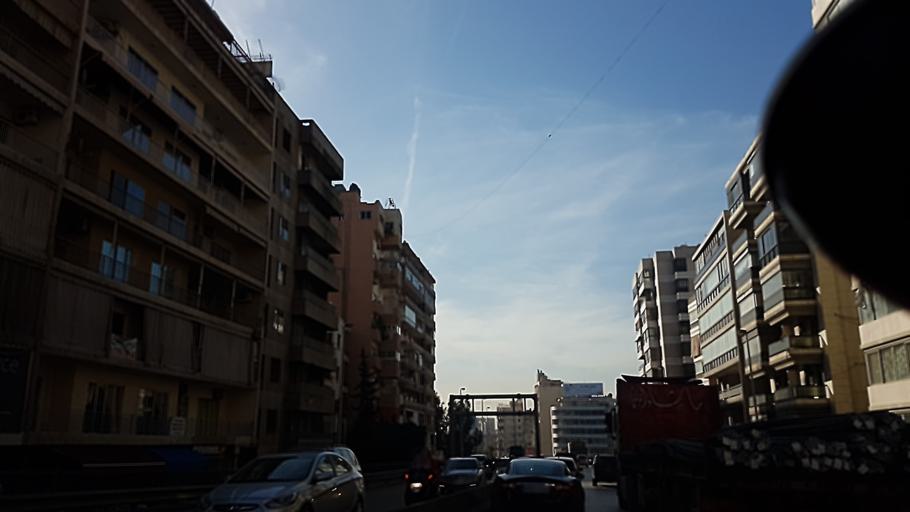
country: LB
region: Beyrouth
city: Beirut
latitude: 33.8813
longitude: 35.4960
